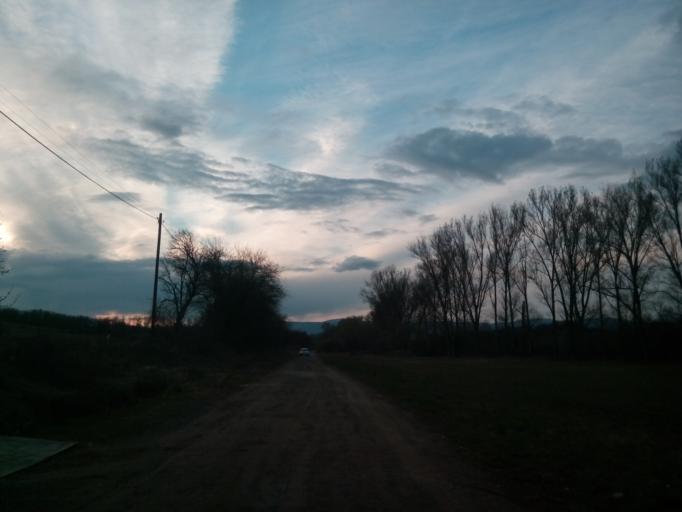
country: SK
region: Kosicky
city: Moldava nad Bodvou
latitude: 48.5486
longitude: 20.9806
